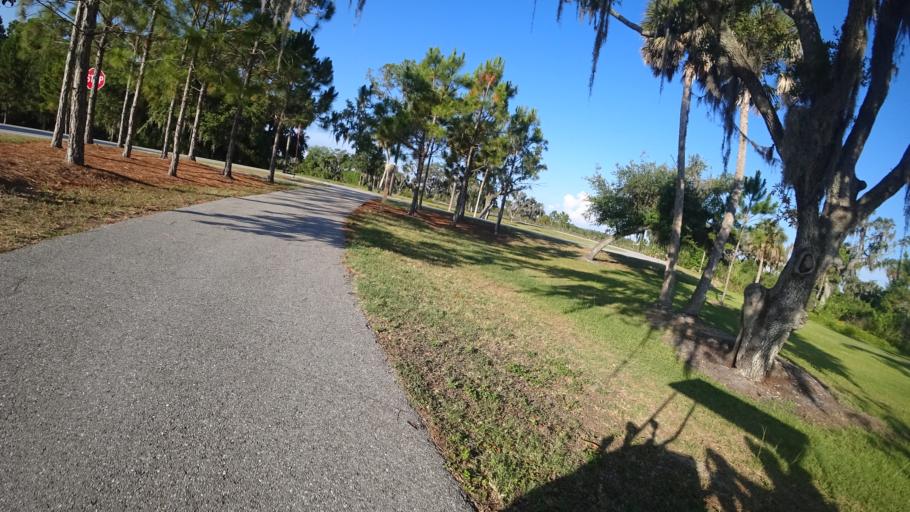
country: US
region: Florida
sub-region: Manatee County
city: Ellenton
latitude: 27.5009
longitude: -82.4853
